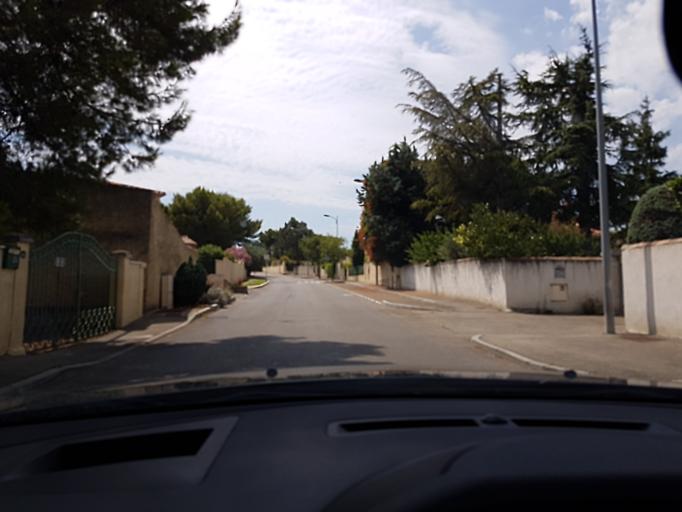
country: FR
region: Provence-Alpes-Cote d'Azur
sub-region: Departement du Vaucluse
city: Saint-Saturnin-les-Avignon
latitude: 43.9619
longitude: 4.9289
